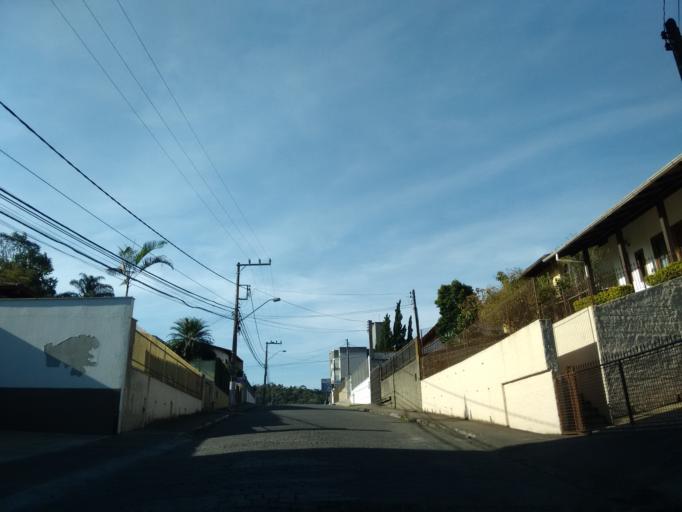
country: BR
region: Santa Catarina
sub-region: Blumenau
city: Blumenau
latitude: -26.8912
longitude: -49.0953
